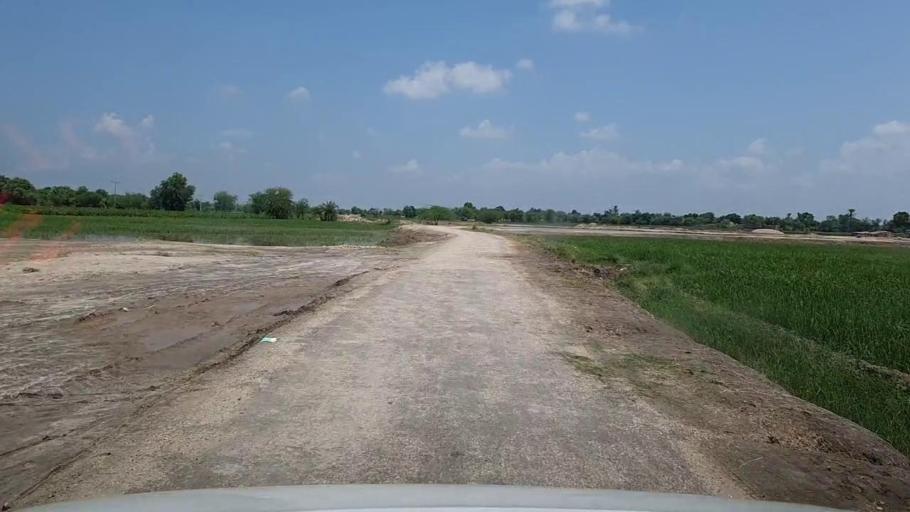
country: PK
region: Sindh
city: Kandiaro
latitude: 26.9864
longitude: 68.2337
